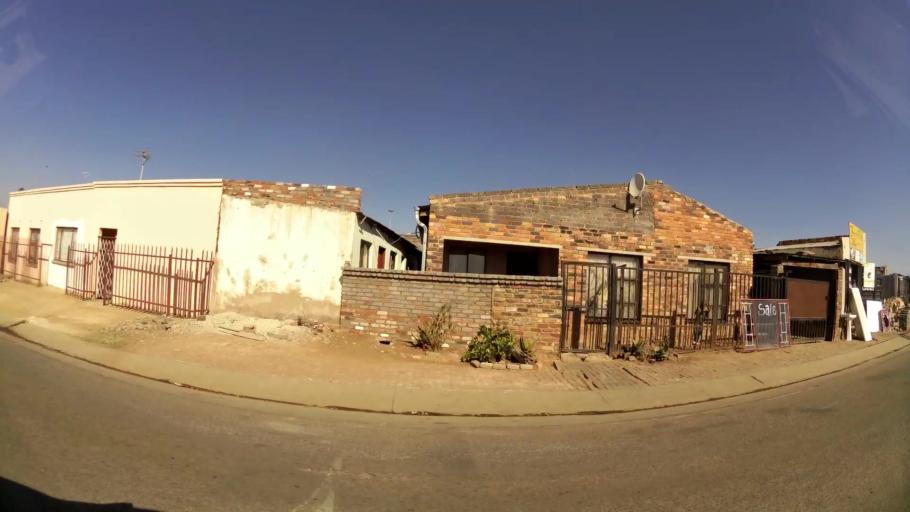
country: ZA
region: Gauteng
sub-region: Ekurhuleni Metropolitan Municipality
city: Tembisa
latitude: -26.0240
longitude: 28.2387
